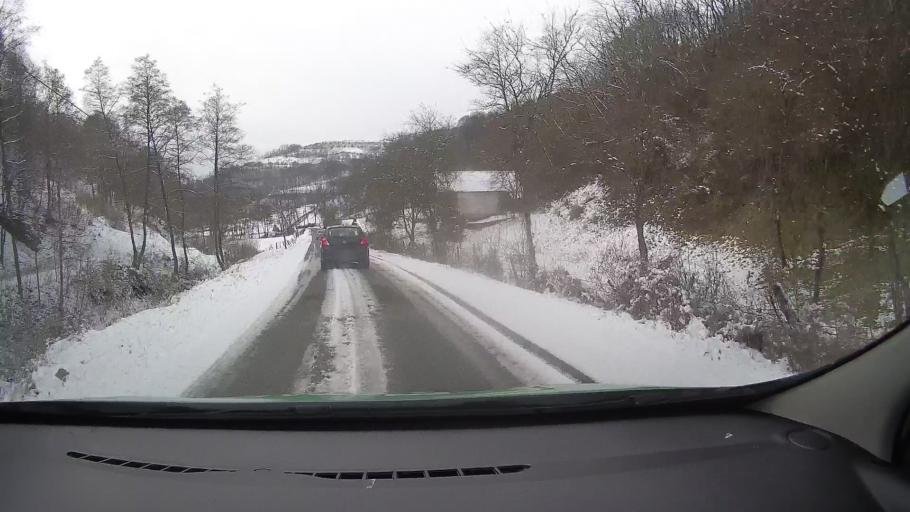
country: RO
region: Alba
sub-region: Comuna Almasu Mare
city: Almasu Mare
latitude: 46.0778
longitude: 23.1109
